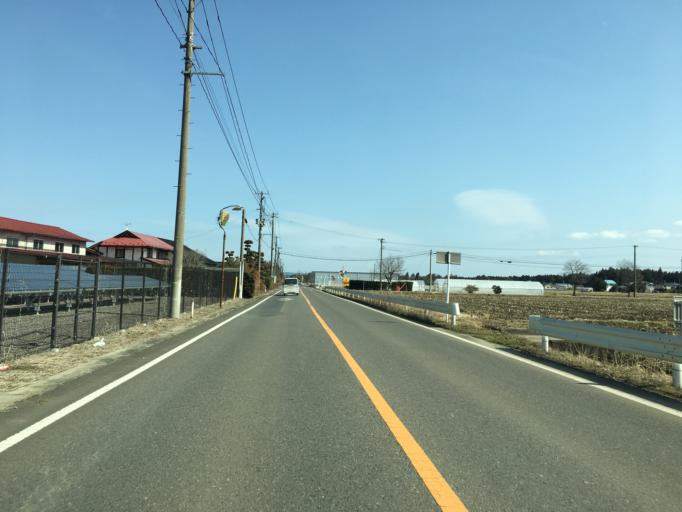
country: JP
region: Fukushima
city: Ishikawa
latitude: 37.1402
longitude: 140.3392
